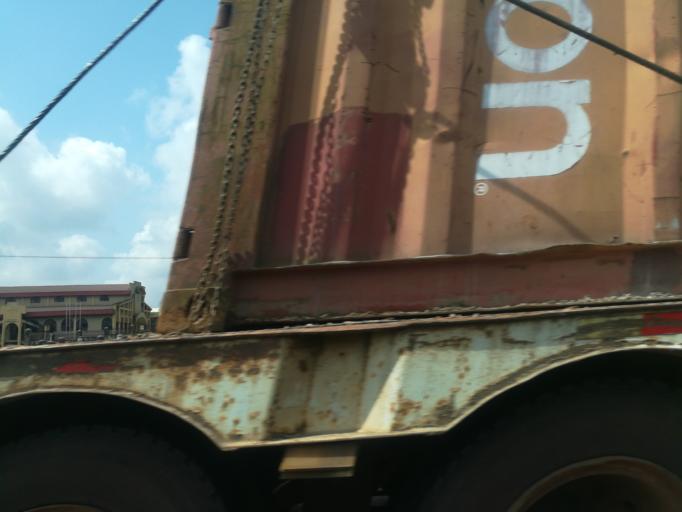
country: NG
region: Oyo
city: Moniya
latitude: 7.4576
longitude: 3.9197
